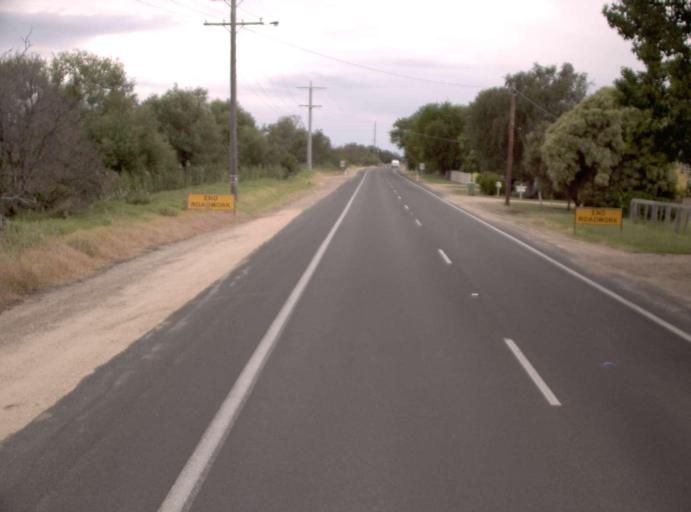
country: AU
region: Victoria
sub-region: East Gippsland
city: Bairnsdale
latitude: -37.8297
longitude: 147.6406
